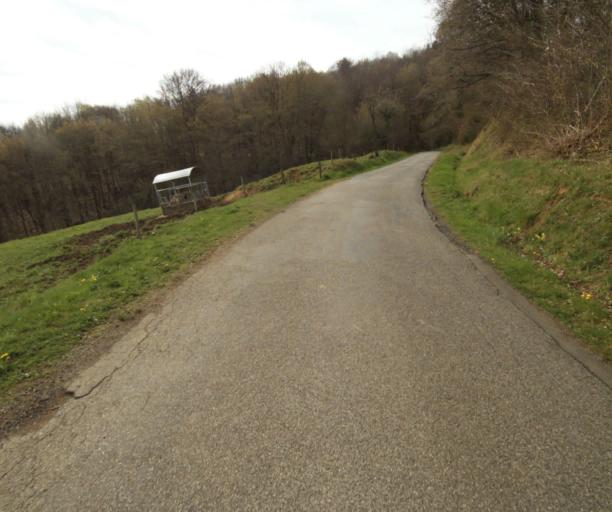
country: FR
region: Limousin
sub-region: Departement de la Correze
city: Laguenne
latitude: 45.2416
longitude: 1.8421
